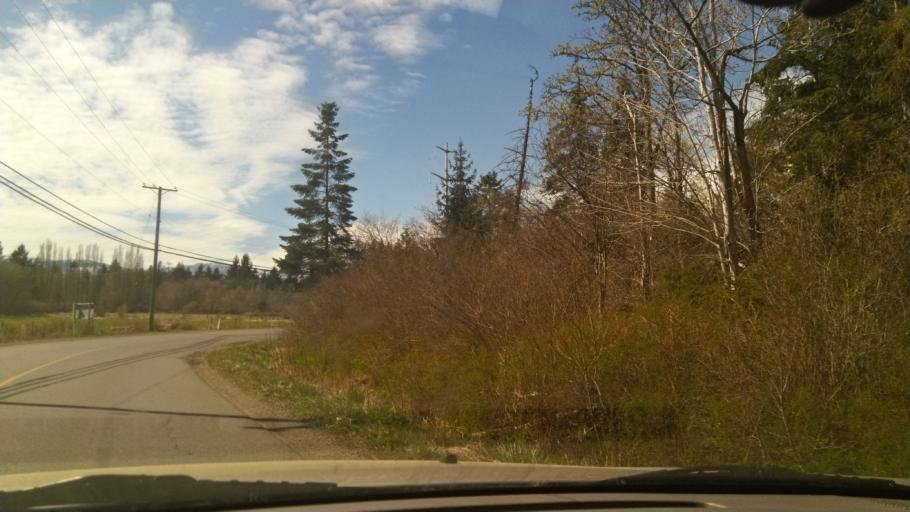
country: CA
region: British Columbia
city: Courtenay
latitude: 49.6956
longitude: -125.0102
